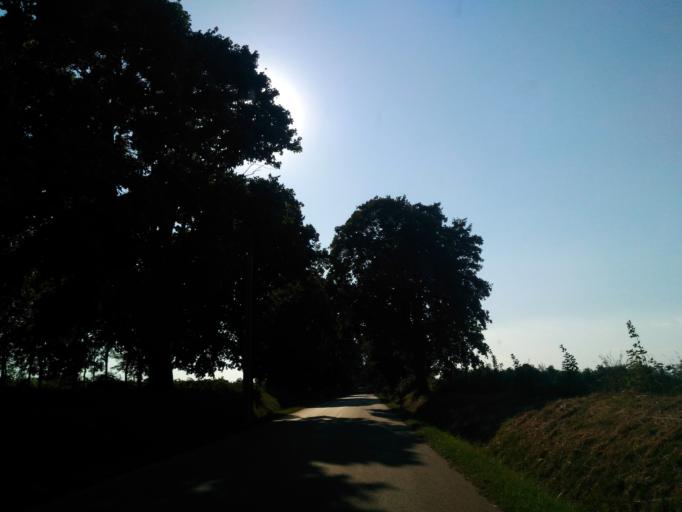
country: HU
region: Somogy
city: Balatonszarszo
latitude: 46.8067
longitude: 17.7915
